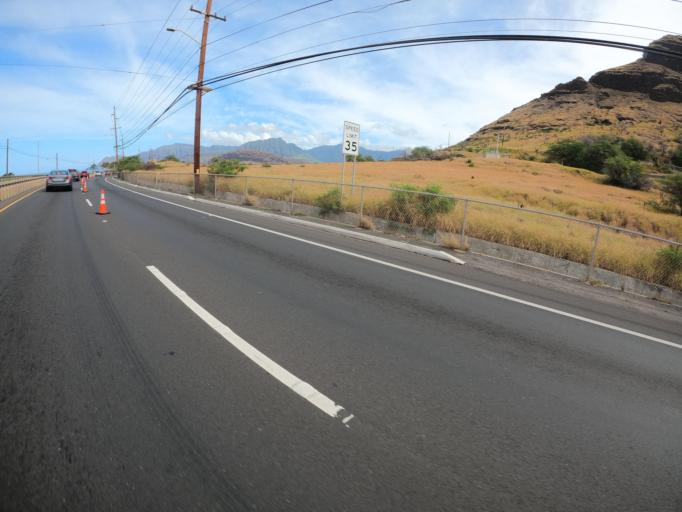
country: US
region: Hawaii
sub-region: Honolulu County
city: Ma'ili
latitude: 21.4021
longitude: -158.1754
